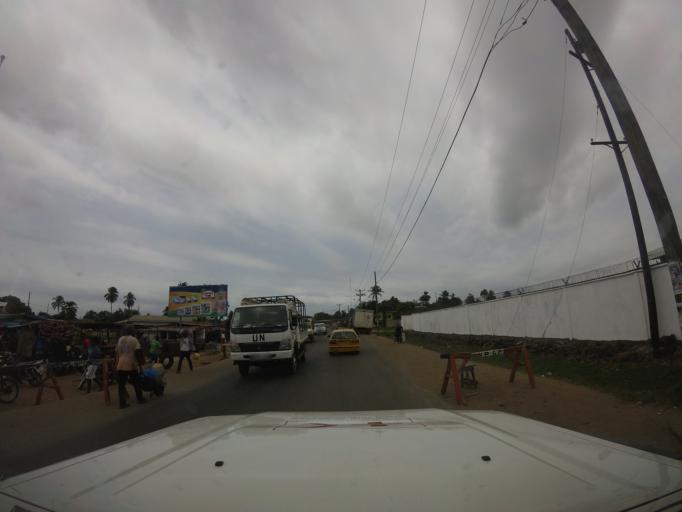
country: LR
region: Montserrado
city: Monrovia
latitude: 6.3776
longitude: -10.7840
